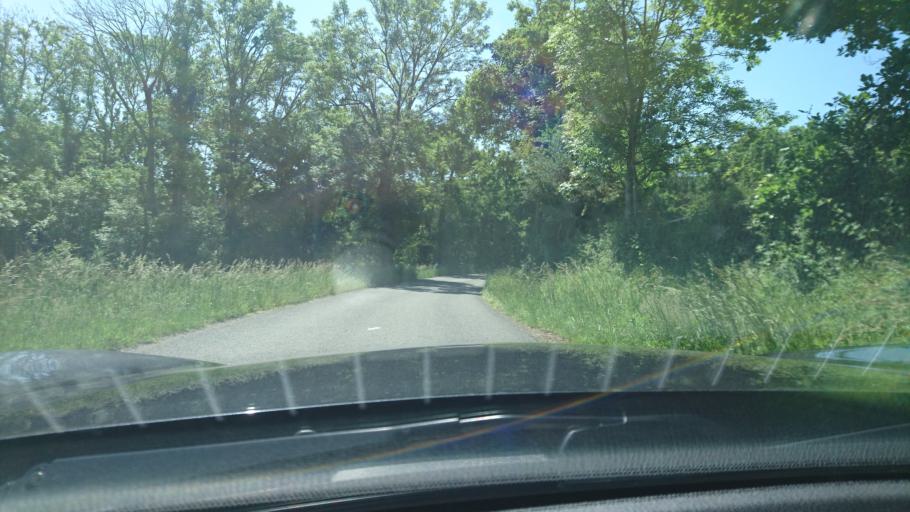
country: FR
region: Rhone-Alpes
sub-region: Departement de la Loire
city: Bussieres
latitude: 45.8717
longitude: 4.2694
